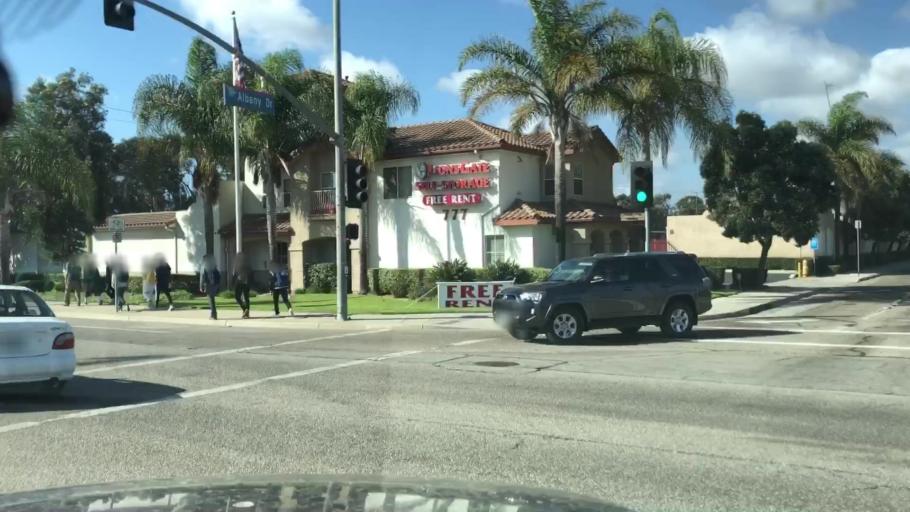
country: US
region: California
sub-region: Ventura County
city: Oxnard
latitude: 34.1734
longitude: -119.1676
